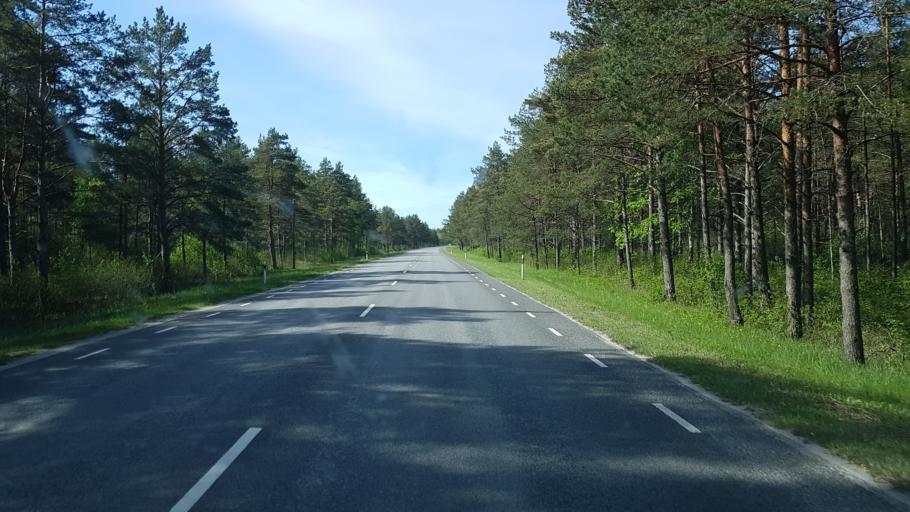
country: EE
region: Saare
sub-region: Orissaare vald
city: Orissaare
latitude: 58.5027
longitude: 22.8652
